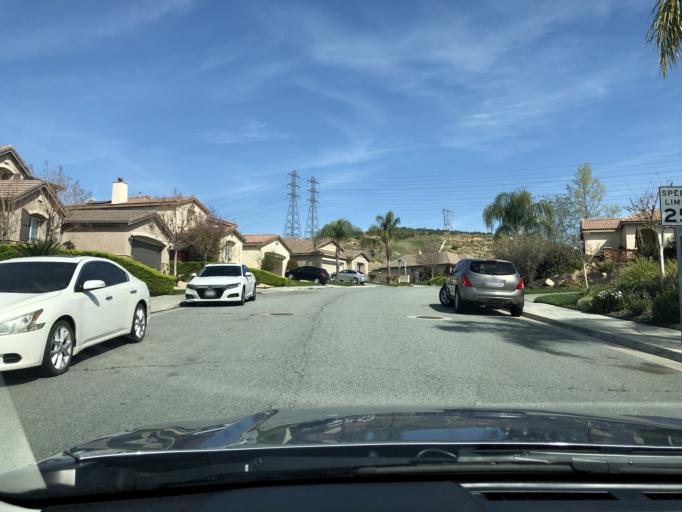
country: US
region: California
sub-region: Riverside County
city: Calimesa
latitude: 33.9616
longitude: -117.0494
